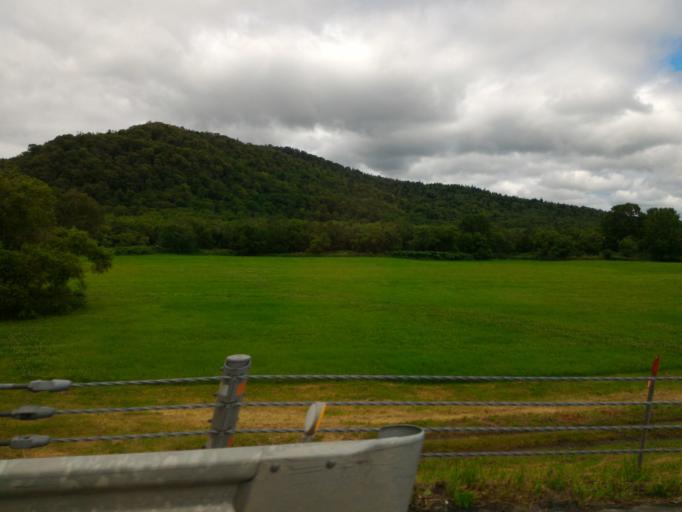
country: JP
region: Hokkaido
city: Nayoro
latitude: 44.7230
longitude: 142.2498
